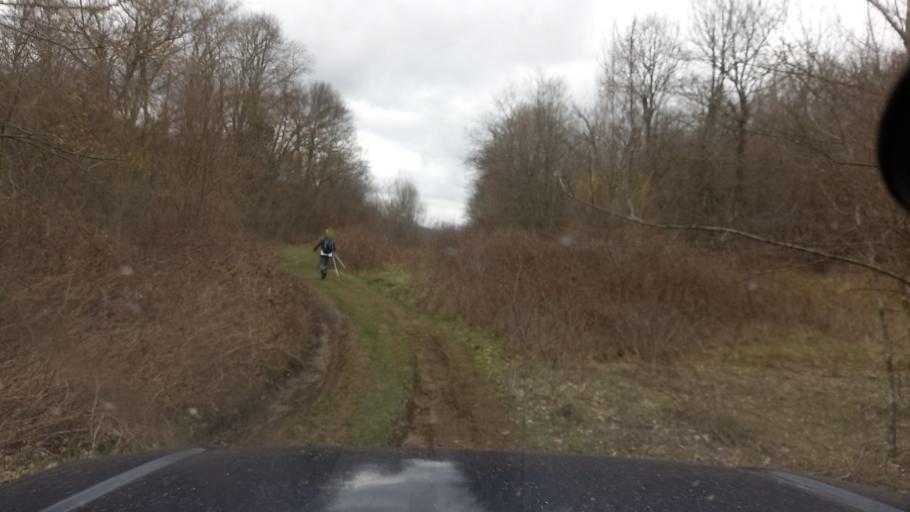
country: RU
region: Krasnodarskiy
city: Pshada
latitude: 44.4867
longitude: 38.3977
